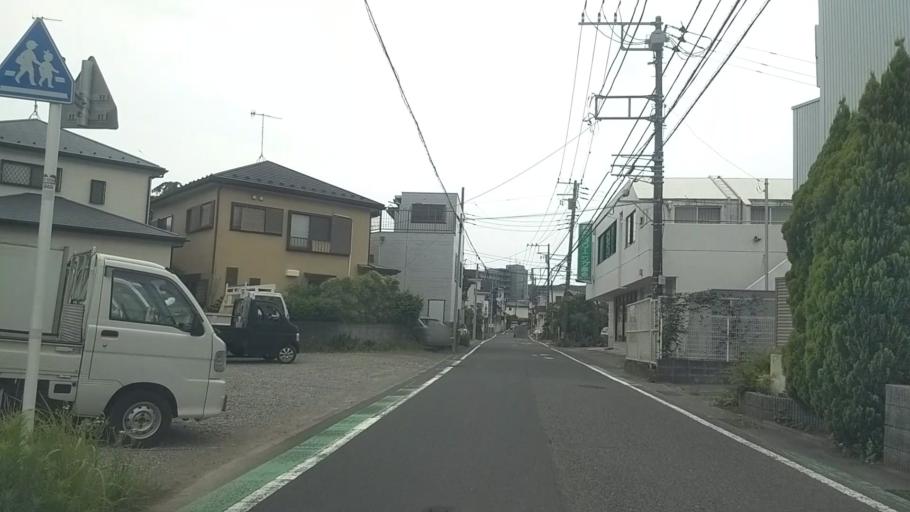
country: JP
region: Kanagawa
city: Fujisawa
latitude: 35.3454
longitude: 139.4556
